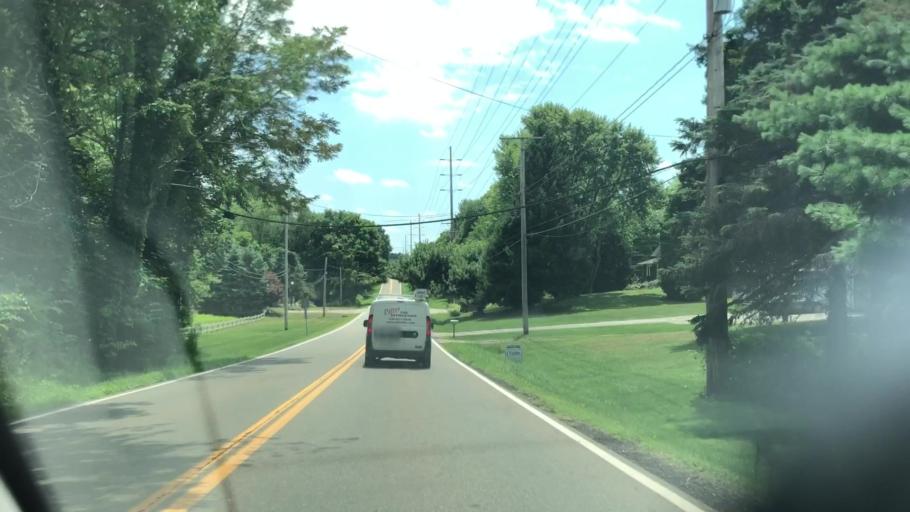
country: US
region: Ohio
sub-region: Summit County
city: Green
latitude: 40.9163
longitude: -81.4967
